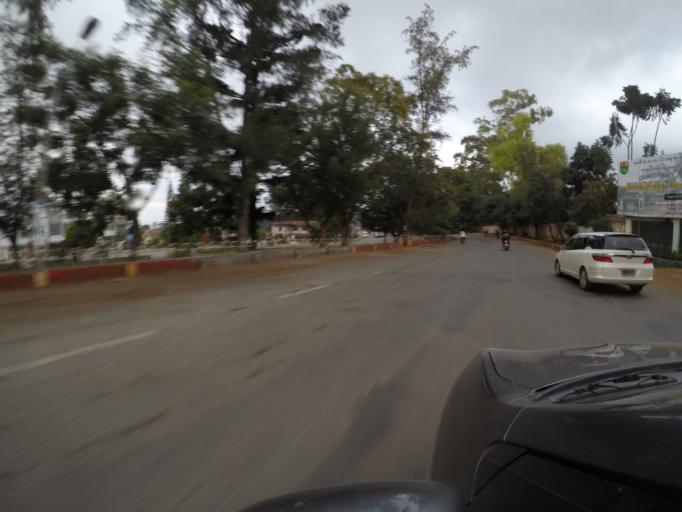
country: MM
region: Shan
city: Taunggyi
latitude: 20.8071
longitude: 97.0354
